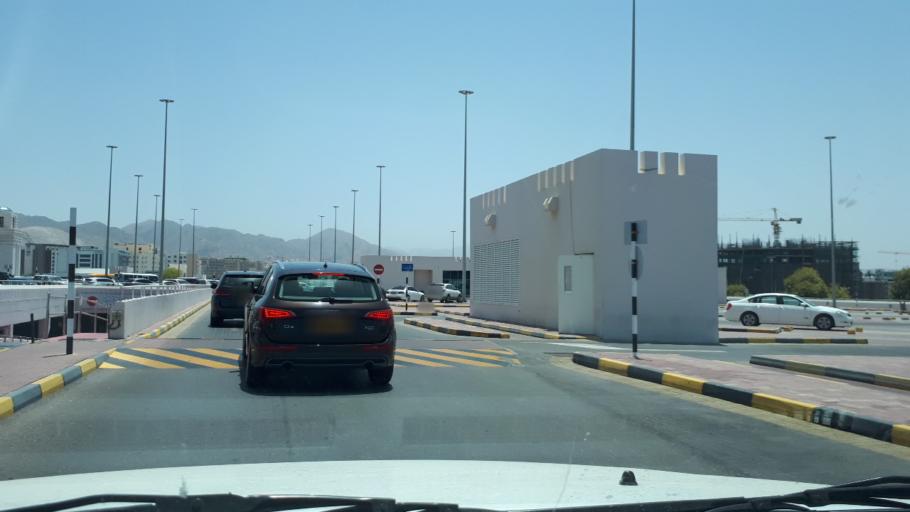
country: OM
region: Muhafazat Masqat
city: Bawshar
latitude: 23.5911
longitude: 58.4102
